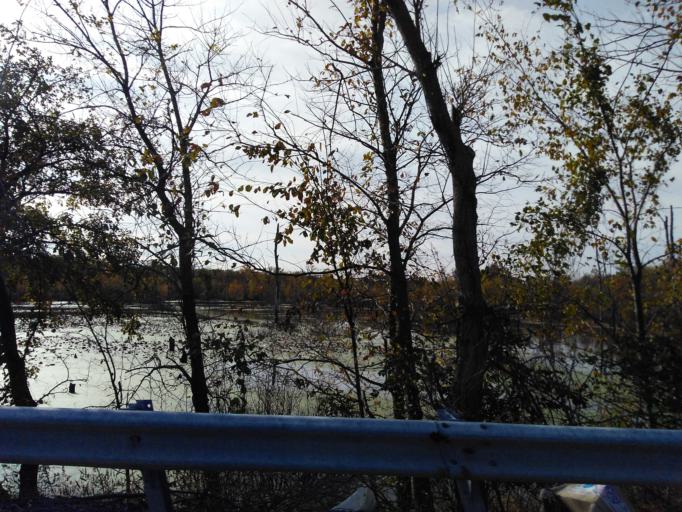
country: US
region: Illinois
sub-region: Madison County
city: Troy
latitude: 38.7168
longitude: -89.8345
